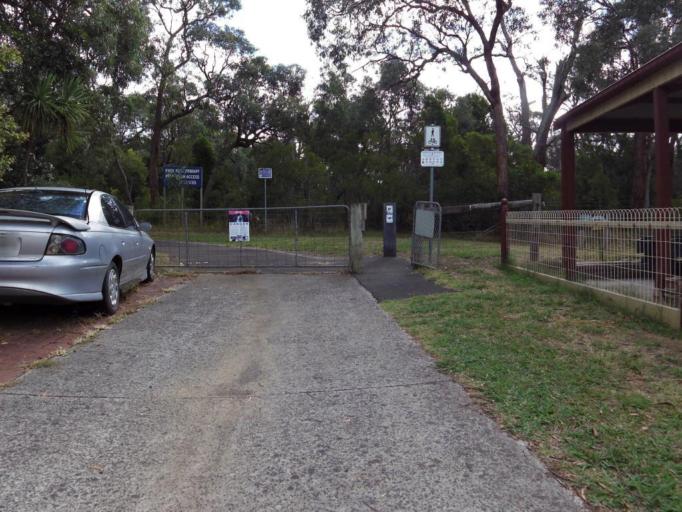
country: AU
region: Victoria
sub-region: Knox
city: Knoxfield
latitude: -37.8820
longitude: 145.2525
